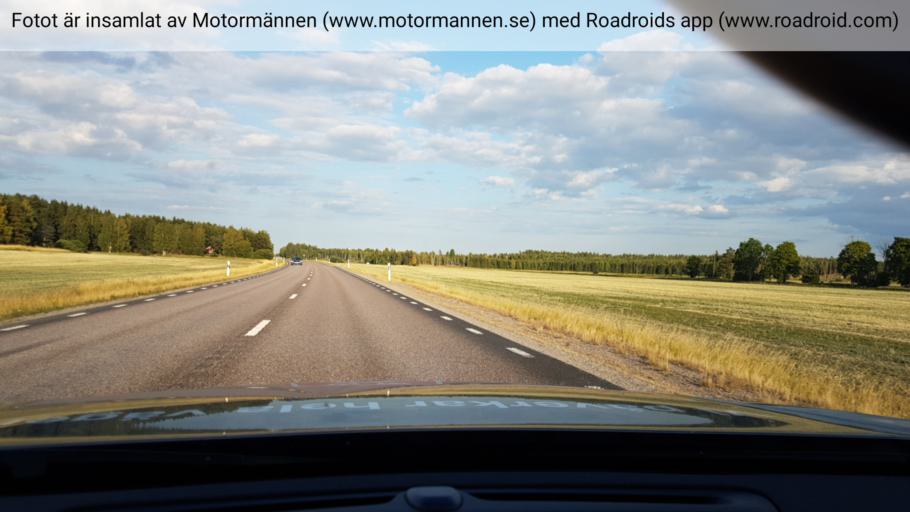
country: SE
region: Uppsala
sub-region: Enkopings Kommun
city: Orsundsbro
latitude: 59.8728
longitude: 17.2992
